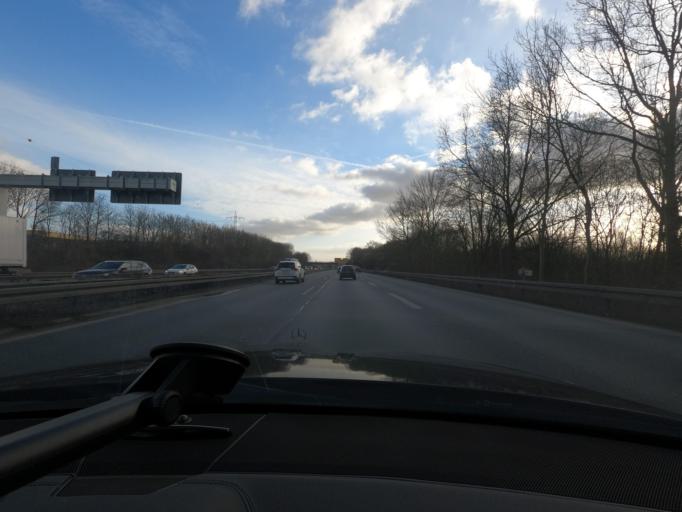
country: DE
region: North Rhine-Westphalia
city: Lunen
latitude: 51.5717
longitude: 7.4987
